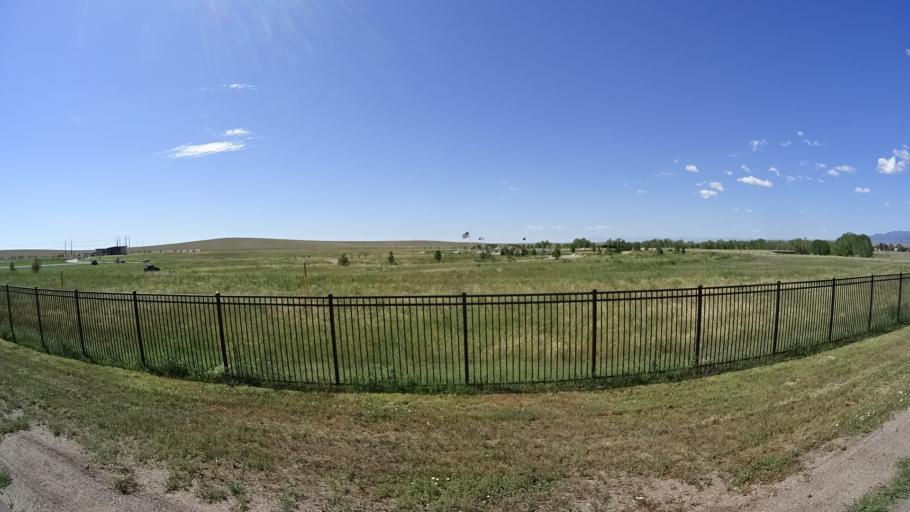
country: US
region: Colorado
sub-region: El Paso County
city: Security-Widefield
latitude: 38.7810
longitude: -104.6367
